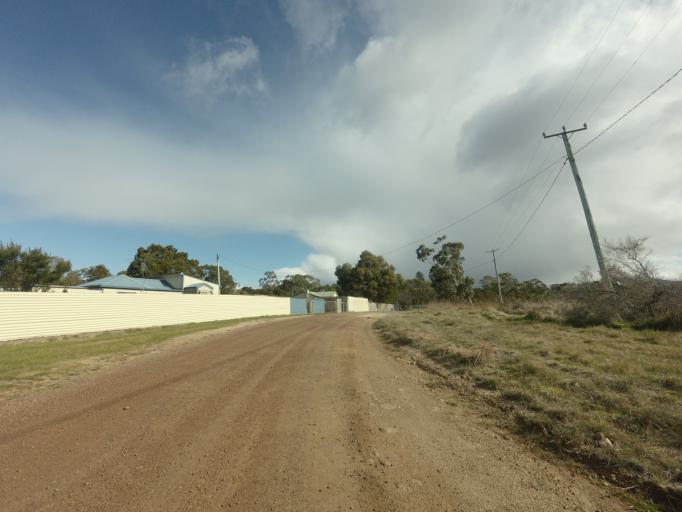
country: AU
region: Tasmania
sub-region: Sorell
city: Sorell
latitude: -42.3252
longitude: 147.9638
